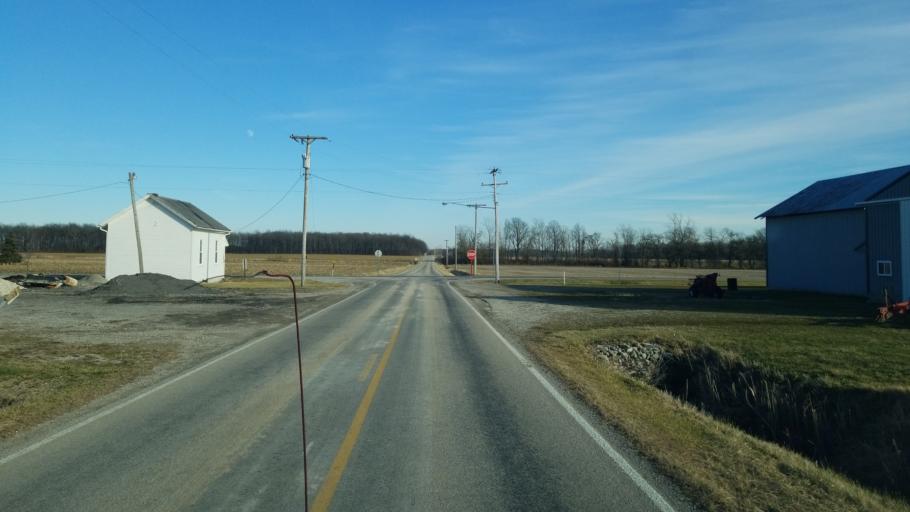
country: US
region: Ohio
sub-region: Huron County
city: Bellevue
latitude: 41.1795
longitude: -82.7884
